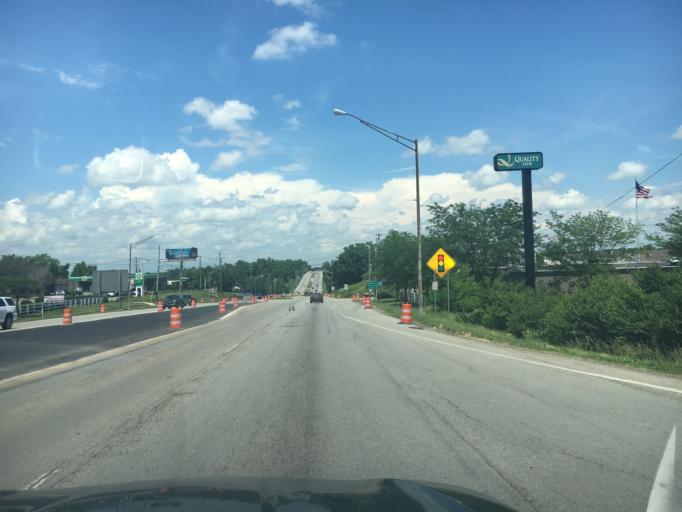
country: US
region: Kentucky
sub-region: Fayette County
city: Lexington-Fayette
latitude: 38.0760
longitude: -84.4945
